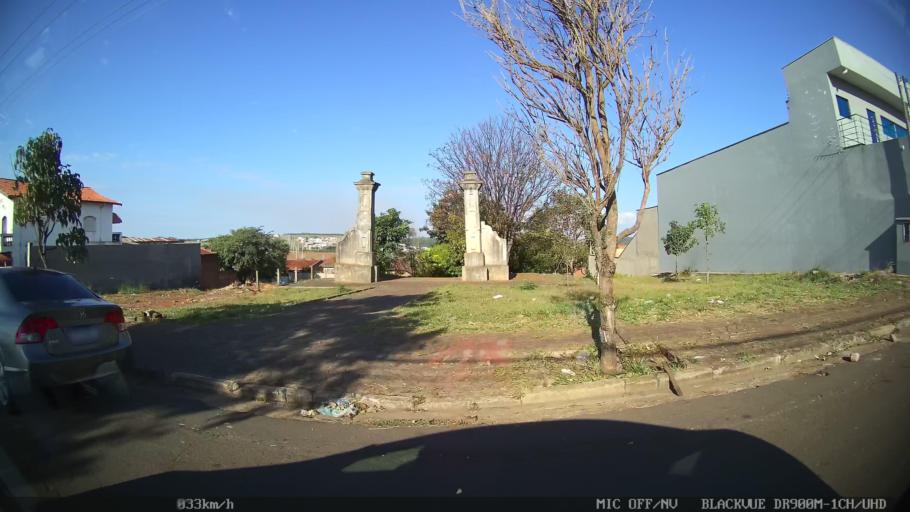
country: BR
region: Sao Paulo
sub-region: Piracicaba
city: Piracicaba
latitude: -22.6853
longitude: -47.6384
